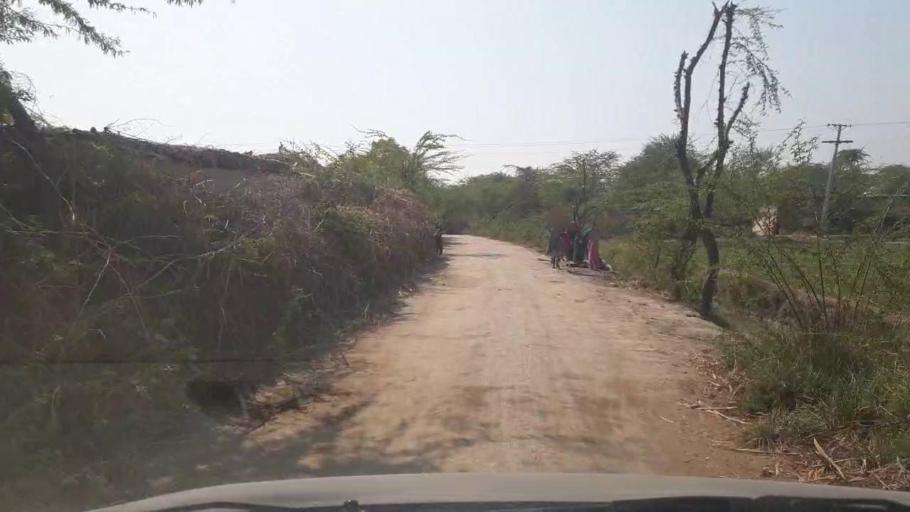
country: PK
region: Sindh
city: Mirwah Gorchani
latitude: 25.2808
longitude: 69.1489
